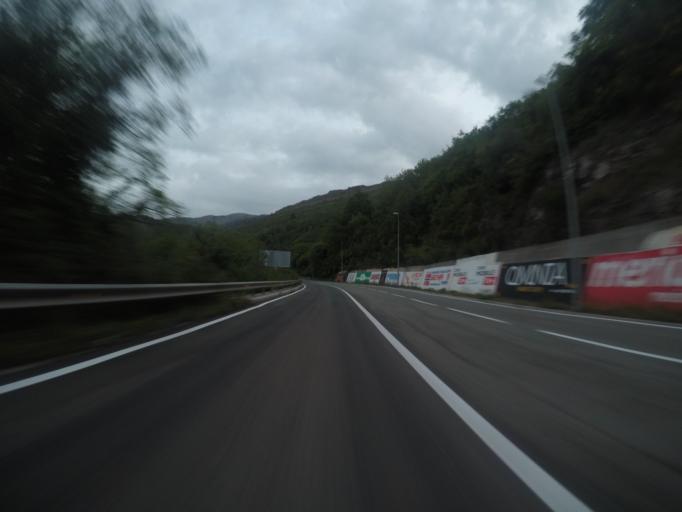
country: ME
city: Petrovac na Moru
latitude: 42.2061
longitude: 18.9498
